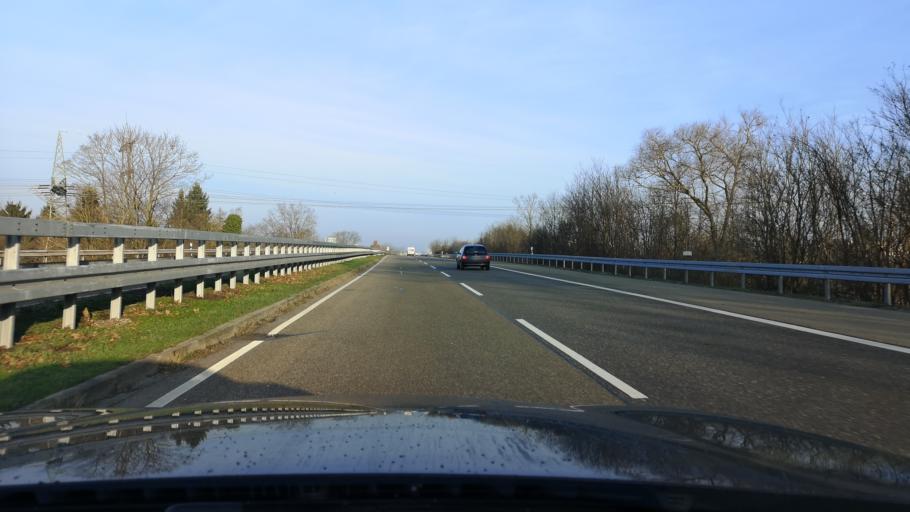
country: DE
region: Baden-Wuerttemberg
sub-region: Karlsruhe Region
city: Karlsruhe
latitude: 48.9777
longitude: 8.3750
